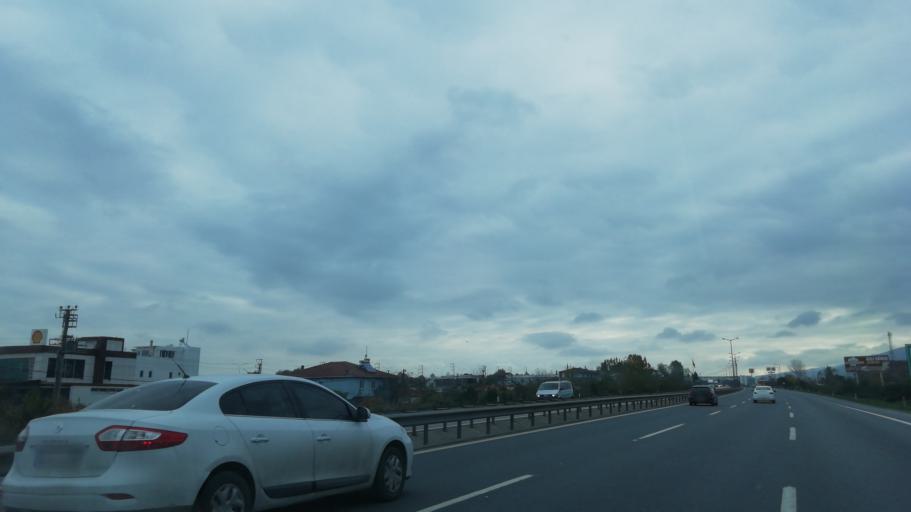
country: TR
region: Kocaeli
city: Derbent
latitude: 40.7302
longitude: 30.0611
